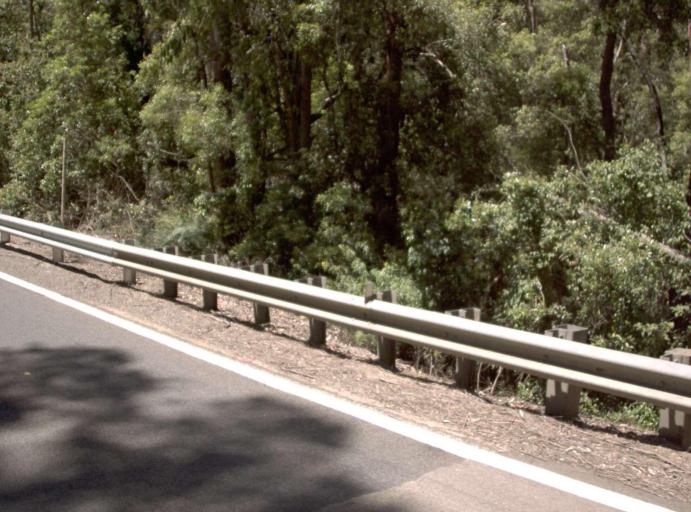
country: AU
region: New South Wales
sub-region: Bombala
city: Bombala
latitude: -37.5907
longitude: 148.9186
